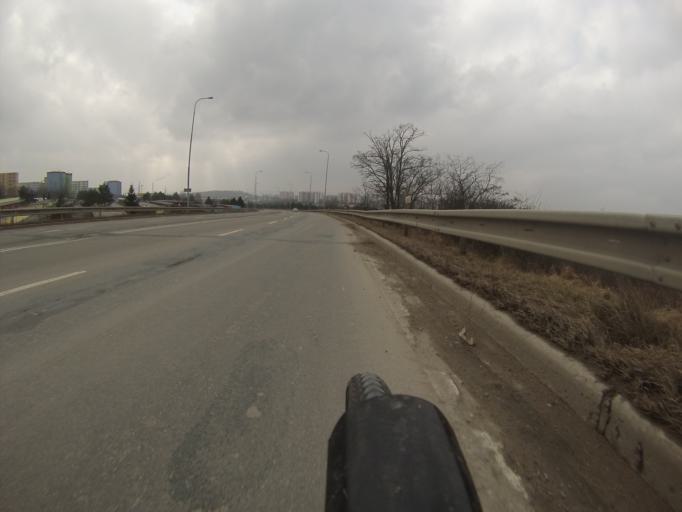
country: CZ
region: South Moravian
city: Bilovice nad Svitavou
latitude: 49.2126
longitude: 16.6748
